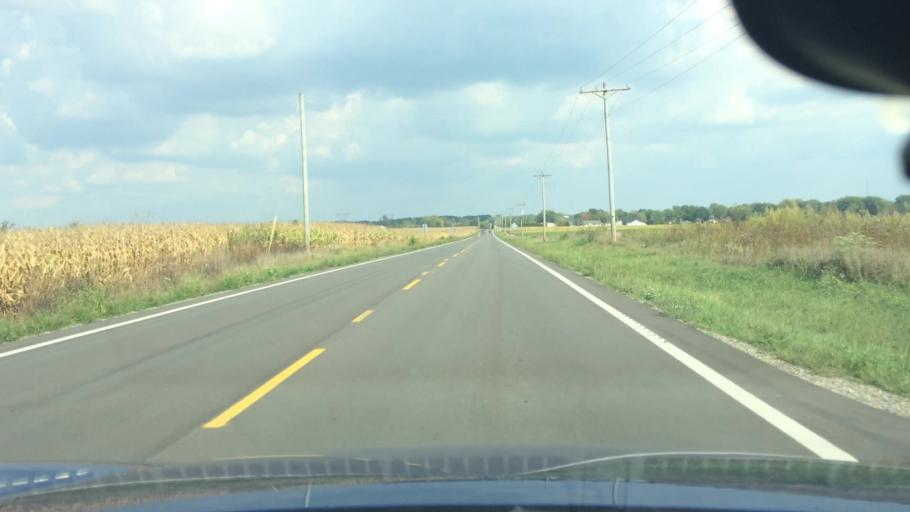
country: US
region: Ohio
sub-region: Logan County
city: Russells Point
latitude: 40.4460
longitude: -83.8184
